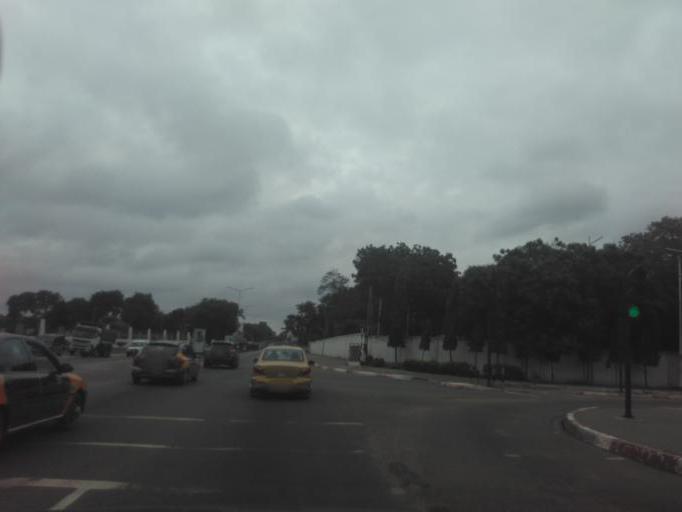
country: GH
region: Greater Accra
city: Accra
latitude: 5.5791
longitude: -0.1866
